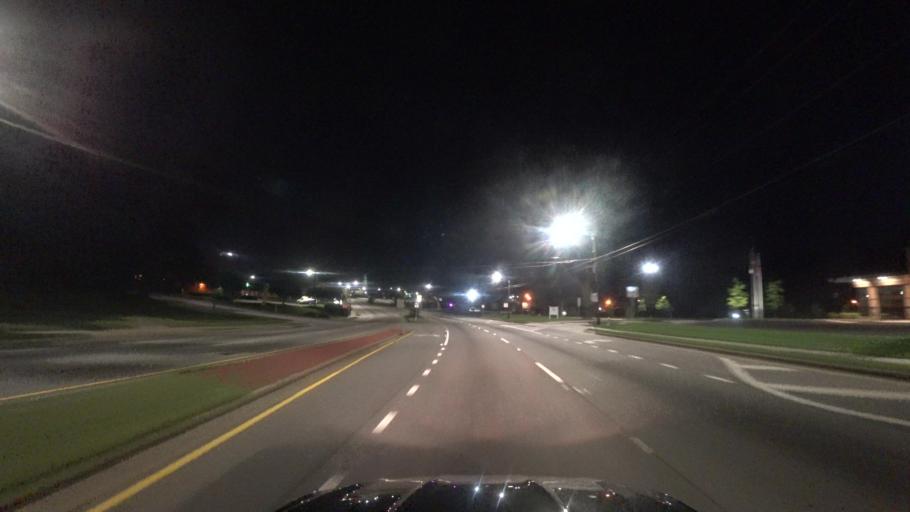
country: US
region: Georgia
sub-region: Clayton County
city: Forest Park
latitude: 33.6206
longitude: -84.3760
